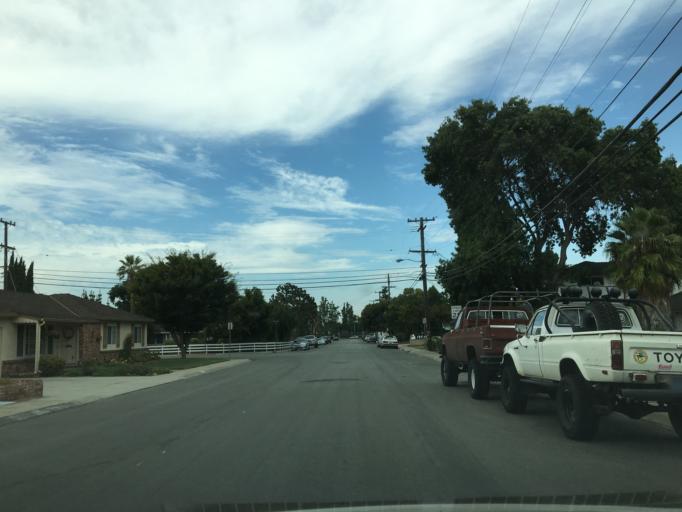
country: US
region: California
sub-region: Santa Clara County
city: Burbank
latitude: 37.3109
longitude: -121.9273
